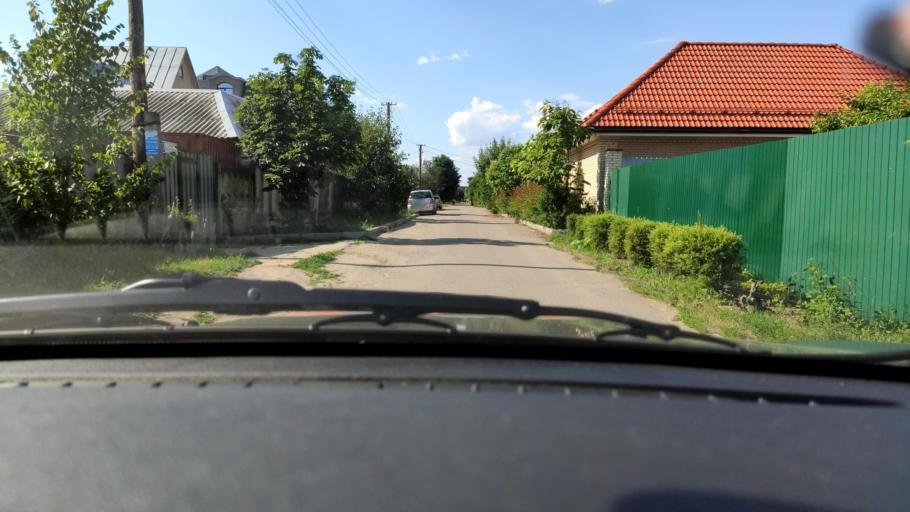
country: RU
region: Voronezj
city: Ramon'
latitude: 51.8311
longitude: 39.2677
